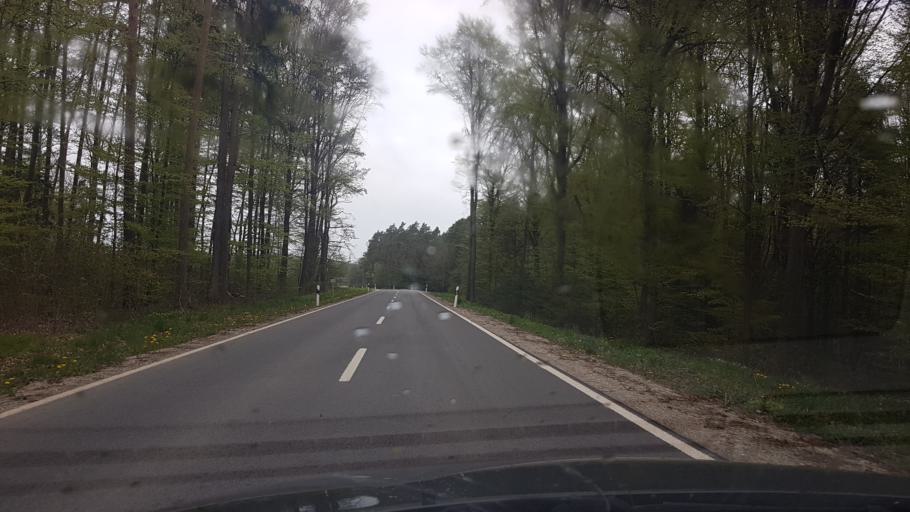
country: DE
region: Bavaria
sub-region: Upper Franconia
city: Konigsfeld
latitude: 49.9865
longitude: 11.1413
